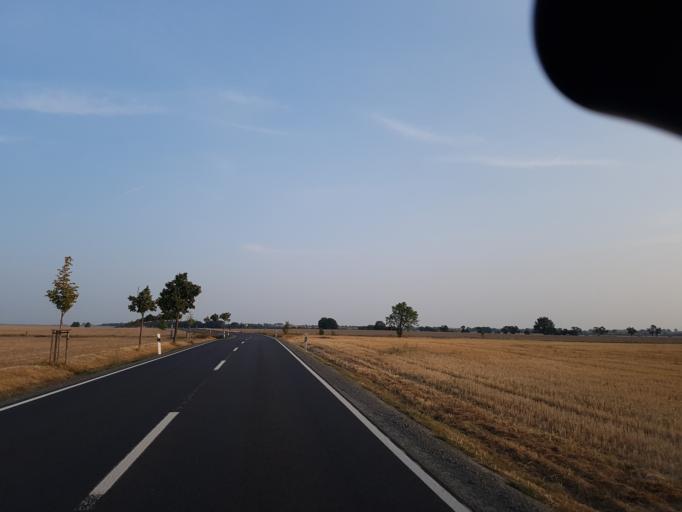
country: DE
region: Saxony
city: Zinna
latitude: 51.5766
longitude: 12.9654
